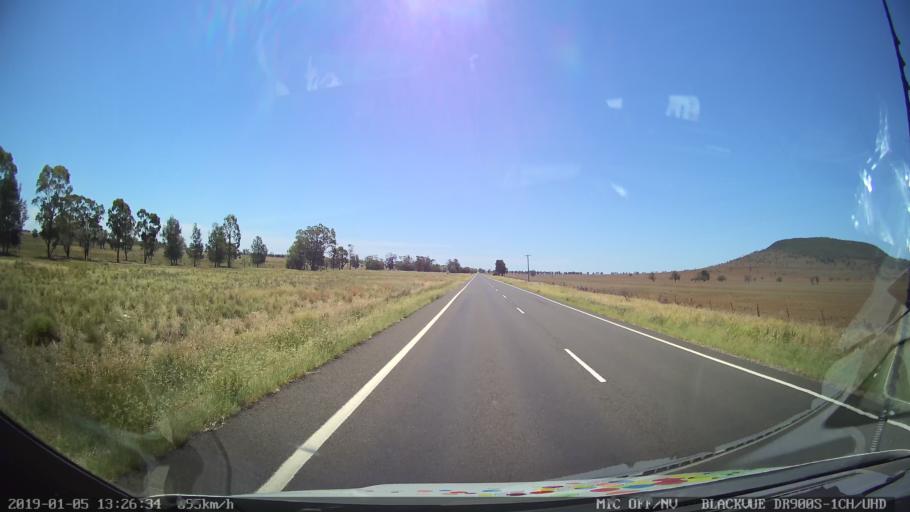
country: AU
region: New South Wales
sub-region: Gunnedah
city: Gunnedah
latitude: -31.0519
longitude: 150.0175
